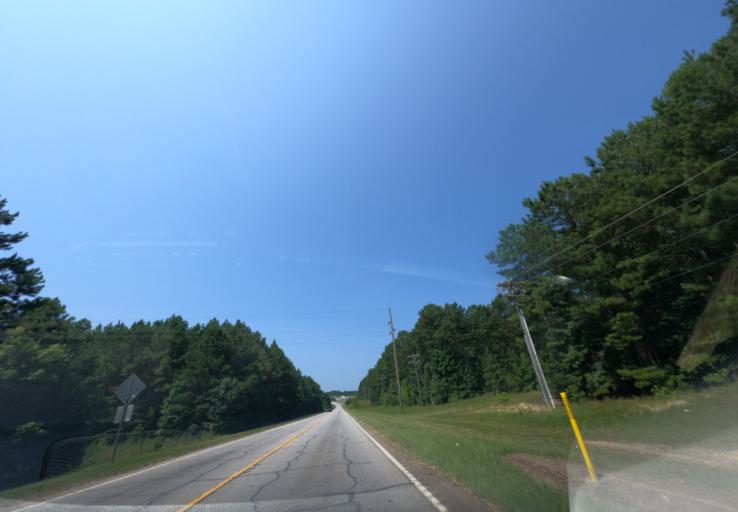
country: US
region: South Carolina
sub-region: Greenwood County
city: Greenwood
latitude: 34.1576
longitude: -82.1325
